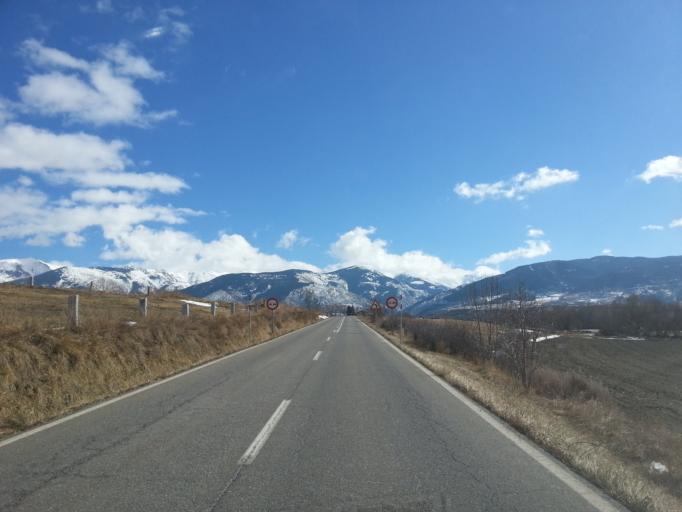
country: ES
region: Catalonia
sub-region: Provincia de Girona
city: Llivia
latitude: 42.4610
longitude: 1.9951
